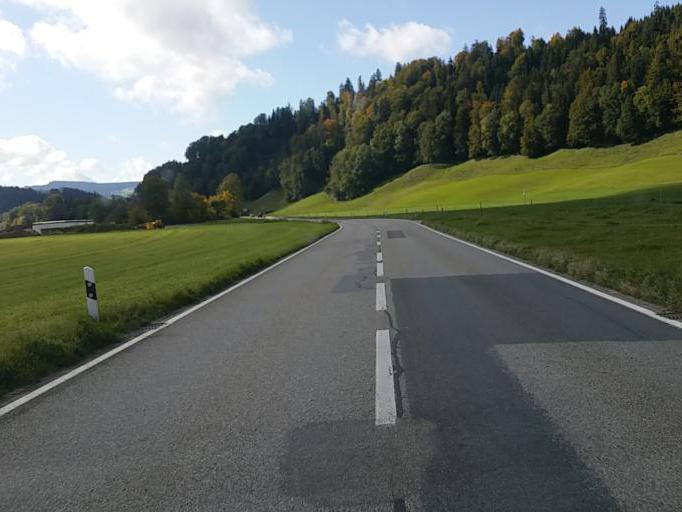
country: CH
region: Bern
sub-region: Emmental District
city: Trachselwald
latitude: 47.0218
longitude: 7.7295
